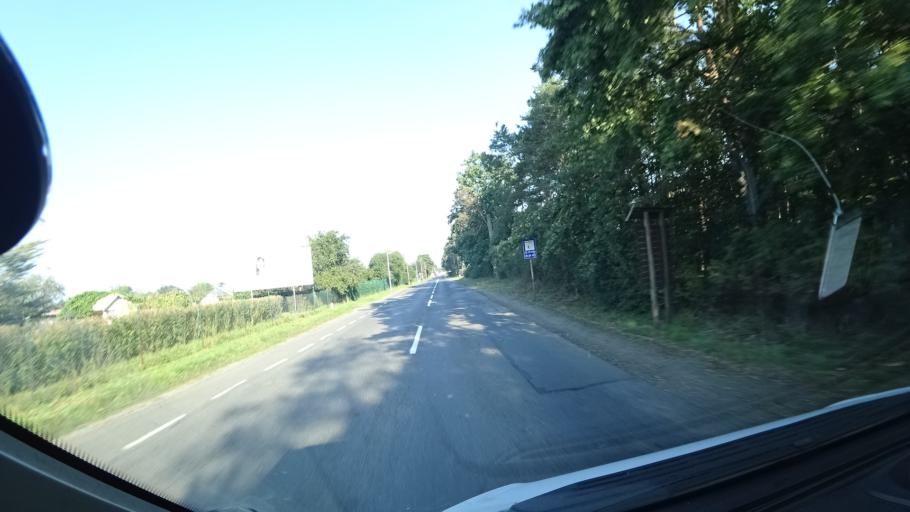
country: PL
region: Opole Voivodeship
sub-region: Powiat kedzierzynsko-kozielski
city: Kedzierzyn-Kozle
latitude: 50.3309
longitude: 18.1970
